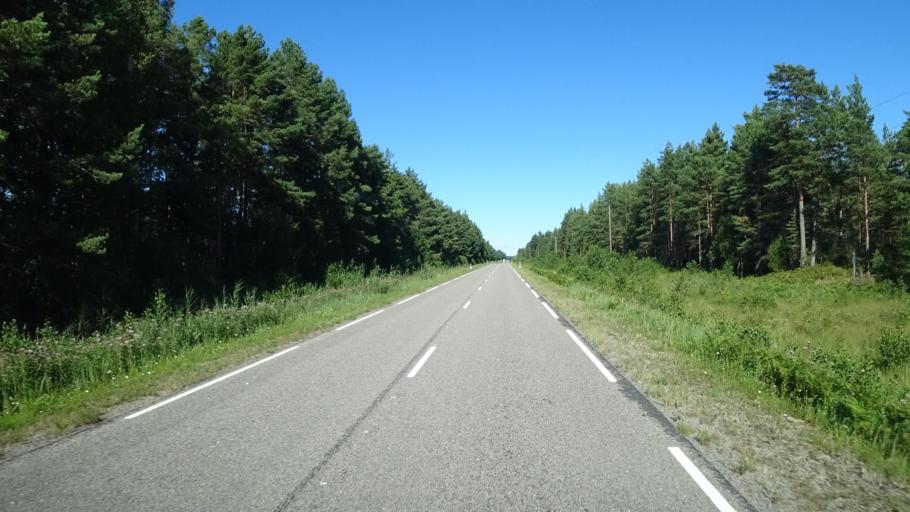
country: LV
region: Dundaga
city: Dundaga
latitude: 57.7041
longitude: 22.4295
